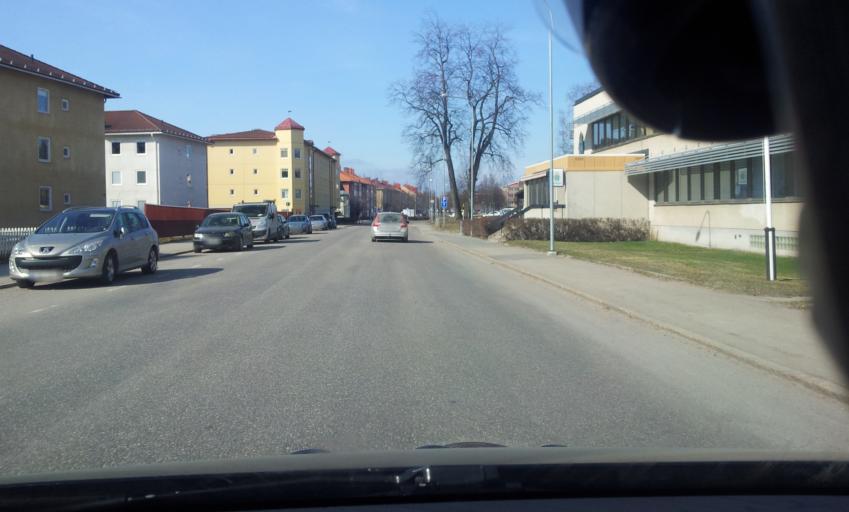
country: SE
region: Gaevleborg
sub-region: Ljusdals Kommun
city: Ljusdal
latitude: 61.8273
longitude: 16.1030
